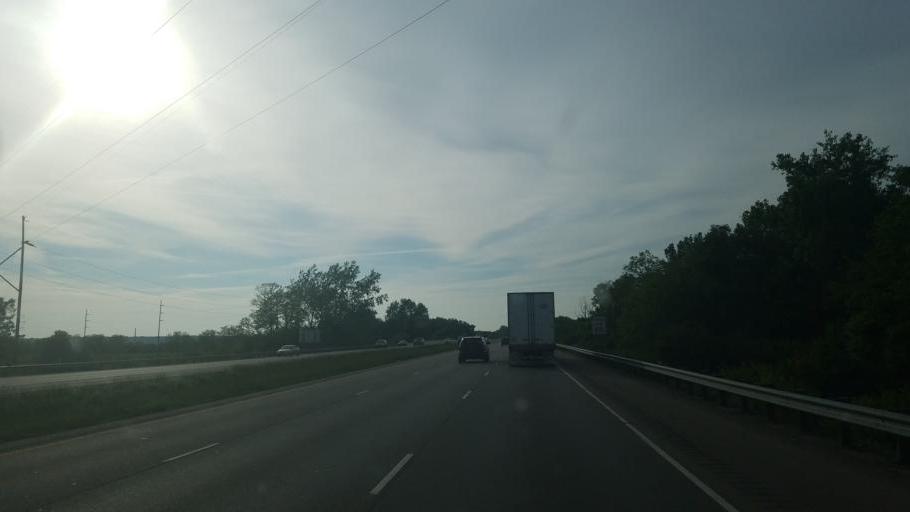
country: US
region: Ohio
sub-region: Ross County
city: Chillicothe
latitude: 39.3432
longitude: -82.9520
